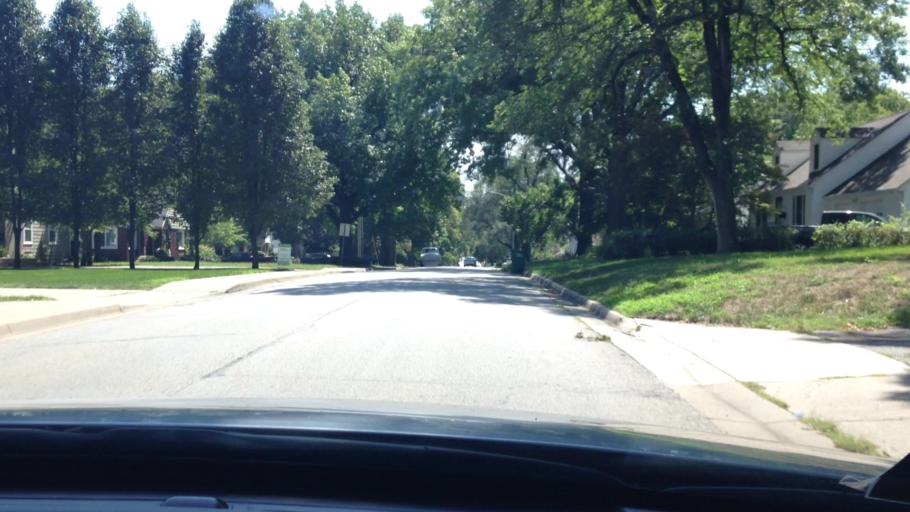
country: US
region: Kansas
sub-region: Johnson County
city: Mission
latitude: 39.0266
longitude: -94.6490
